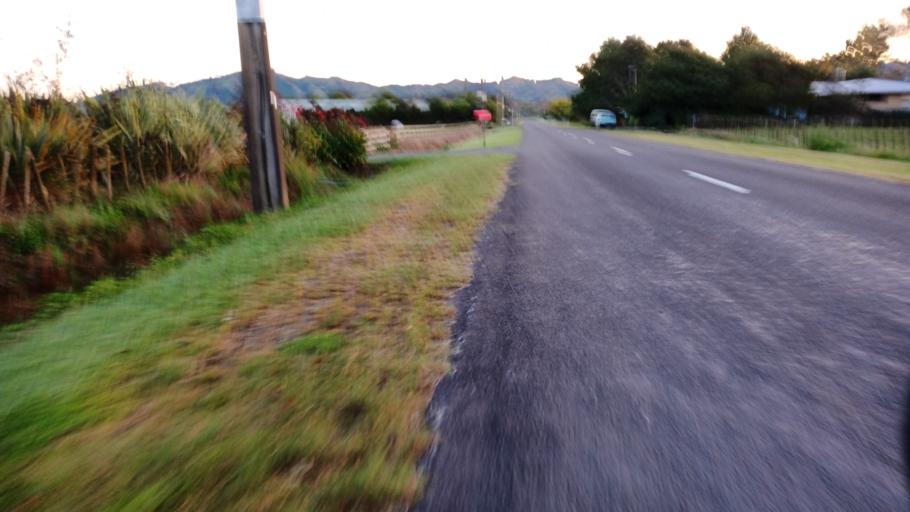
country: NZ
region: Gisborne
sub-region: Gisborne District
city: Gisborne
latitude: -38.6380
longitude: 177.9846
